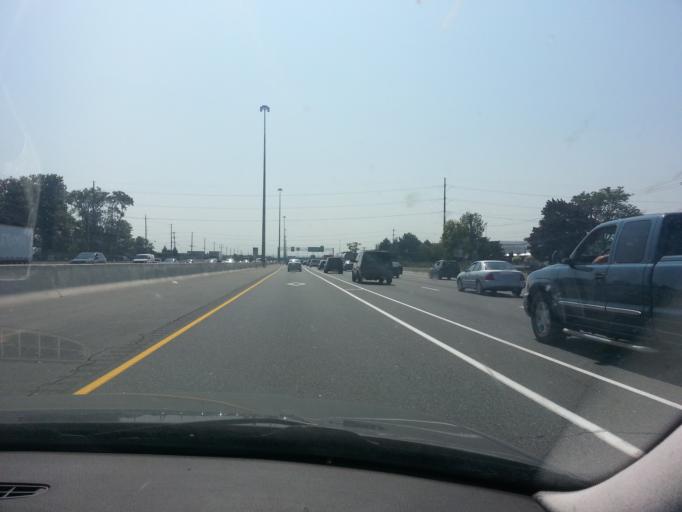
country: CA
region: Ontario
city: Burlington
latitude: 43.3599
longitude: -79.7954
